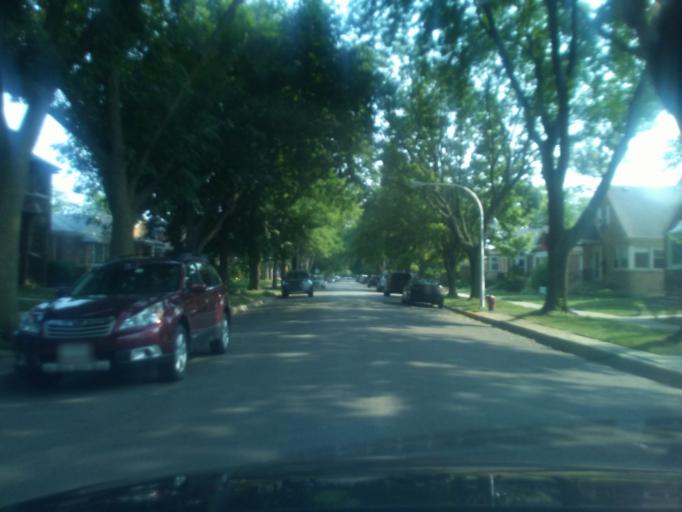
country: US
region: Illinois
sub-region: Cook County
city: Lincolnwood
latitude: 41.9946
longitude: -87.7362
